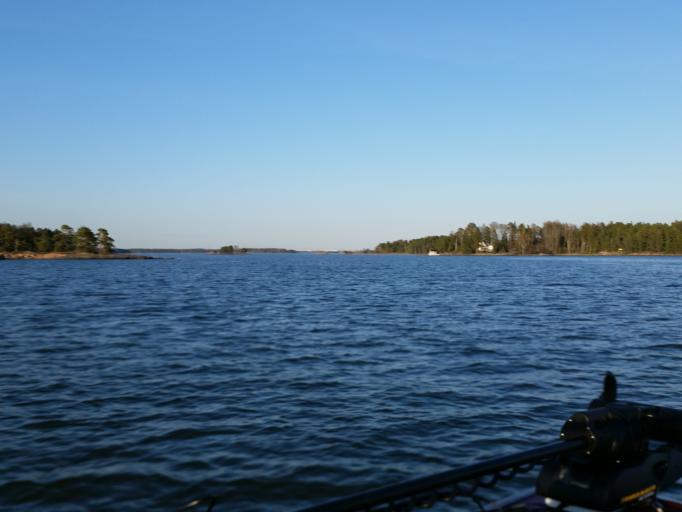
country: FI
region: Uusimaa
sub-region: Helsinki
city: Koukkuniemi
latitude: 60.1351
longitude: 24.7556
